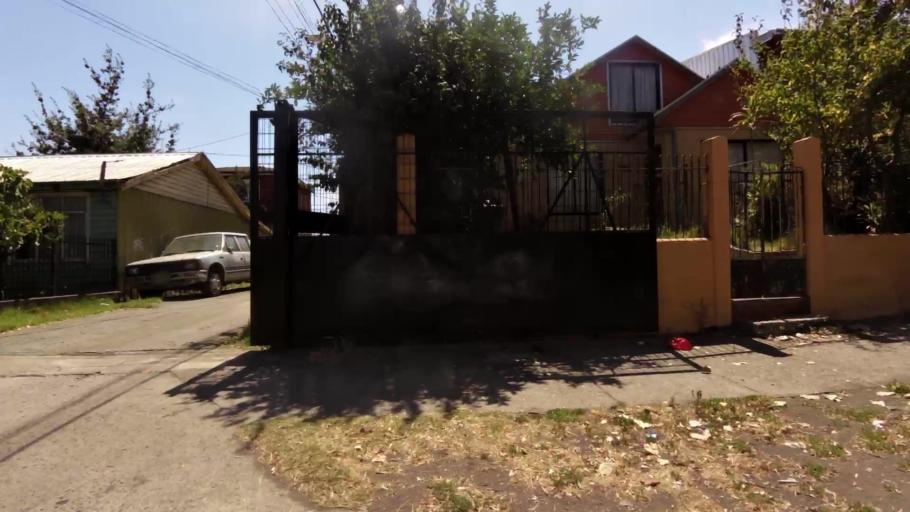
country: CL
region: Biobio
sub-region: Provincia de Concepcion
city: Concepcion
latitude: -36.8070
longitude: -73.0444
